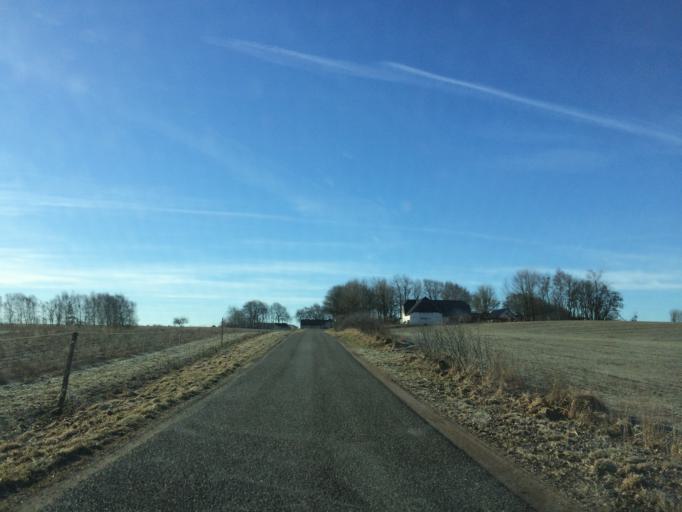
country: DK
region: North Denmark
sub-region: Mariagerfjord Kommune
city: Hobro
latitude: 56.6410
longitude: 9.6424
